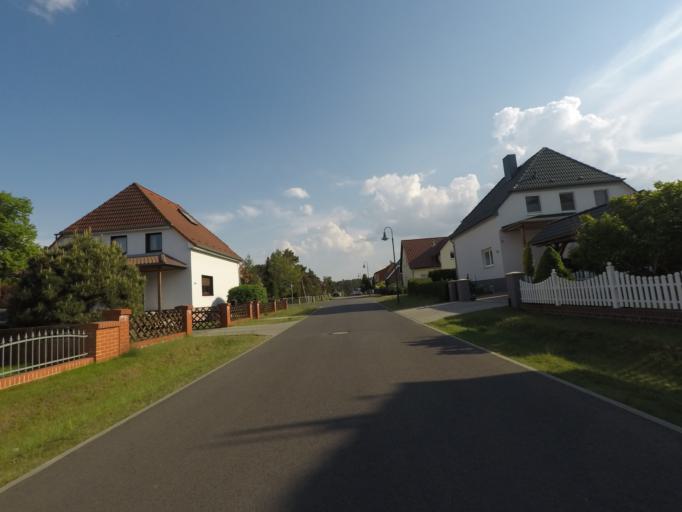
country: DE
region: Brandenburg
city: Melchow
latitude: 52.8360
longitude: 13.7210
